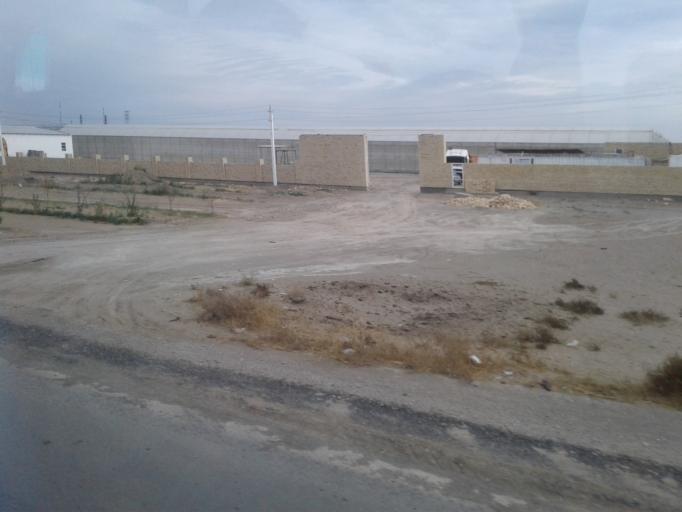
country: TM
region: Lebap
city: Turkmenabat
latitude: 39.0004
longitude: 63.5309
